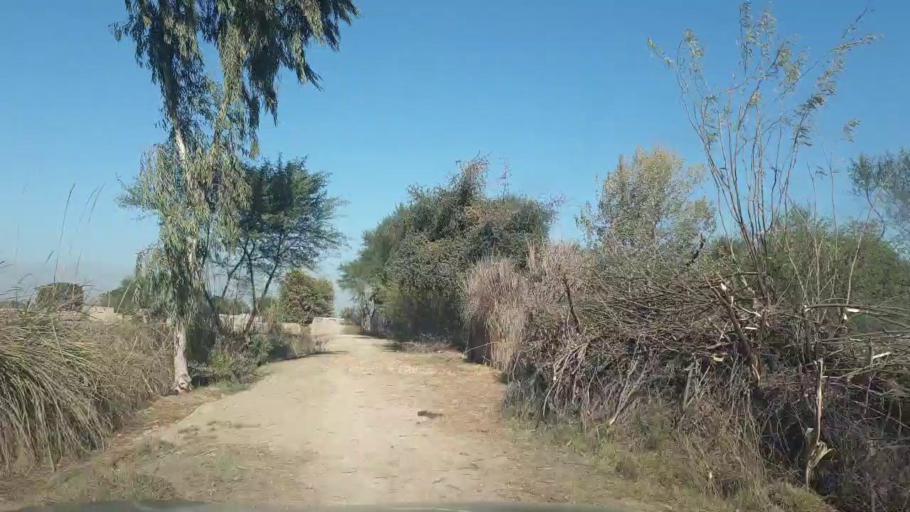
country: PK
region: Sindh
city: Mirpur Mathelo
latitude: 28.0608
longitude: 69.5101
